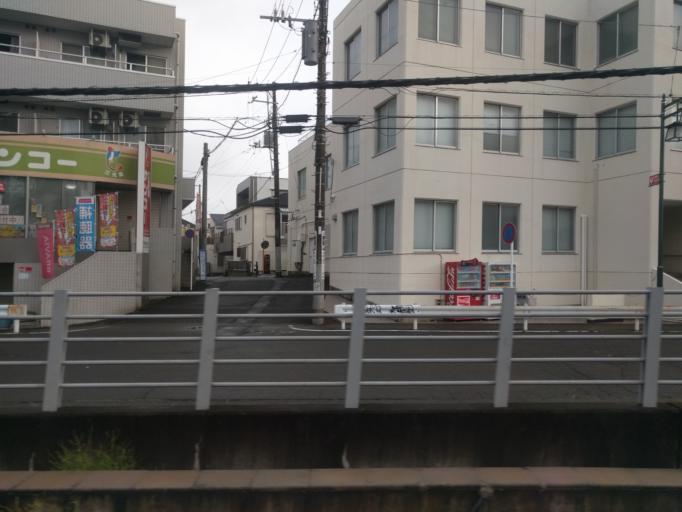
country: JP
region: Tokyo
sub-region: Machida-shi
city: Machida
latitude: 35.5319
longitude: 139.4972
